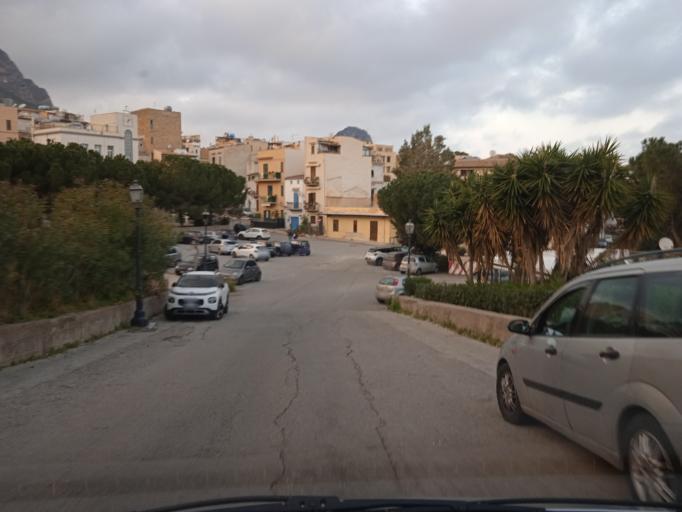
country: IT
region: Sicily
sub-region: Palermo
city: Santa Flavia
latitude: 38.0950
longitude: 13.5385
